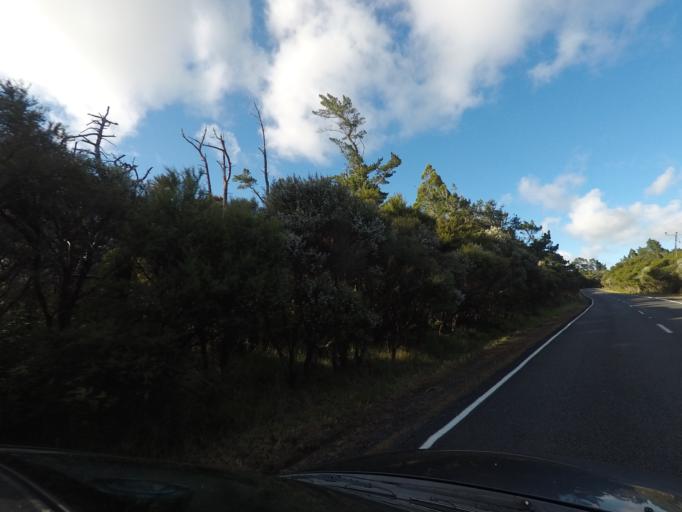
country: NZ
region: Auckland
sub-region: Auckland
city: Titirangi
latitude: -36.9944
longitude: 174.6004
